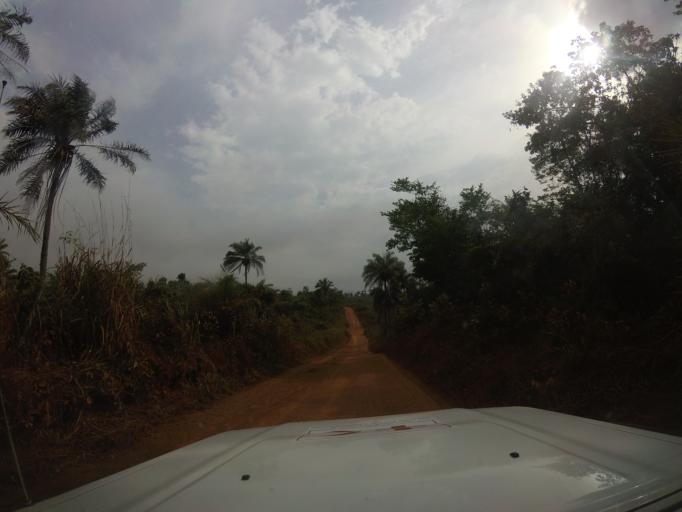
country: LR
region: Grand Cape Mount
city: Robertsport
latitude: 7.0114
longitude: -11.2898
